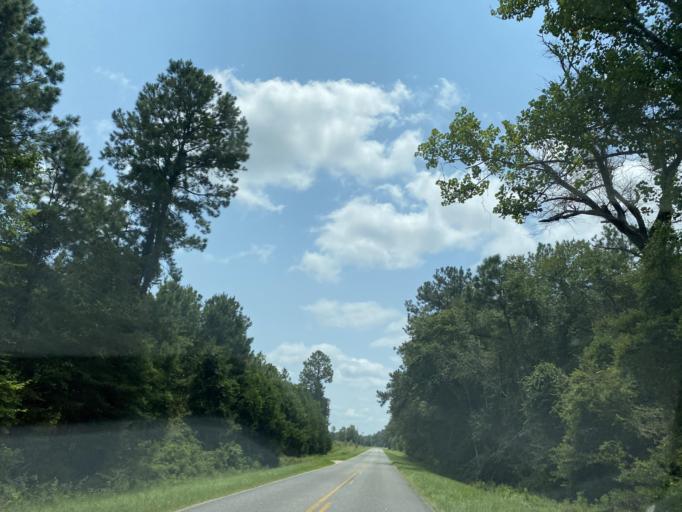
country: US
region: Georgia
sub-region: Telfair County
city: Lumber City
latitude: 31.9861
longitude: -82.7019
